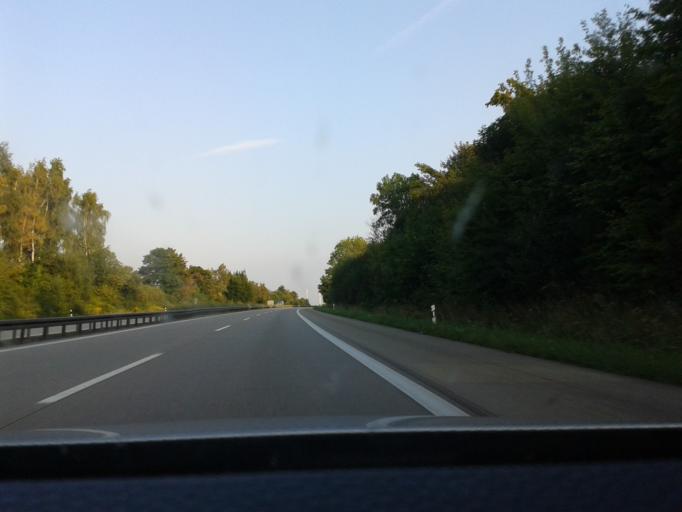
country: DE
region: Saxony
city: Dobeln
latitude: 51.1501
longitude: 13.1397
